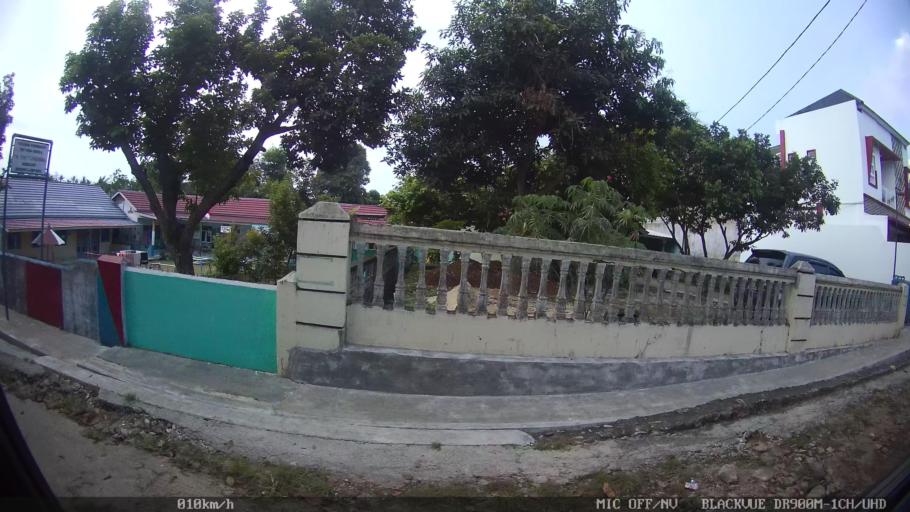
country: ID
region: Lampung
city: Kedaton
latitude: -5.3946
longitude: 105.2062
